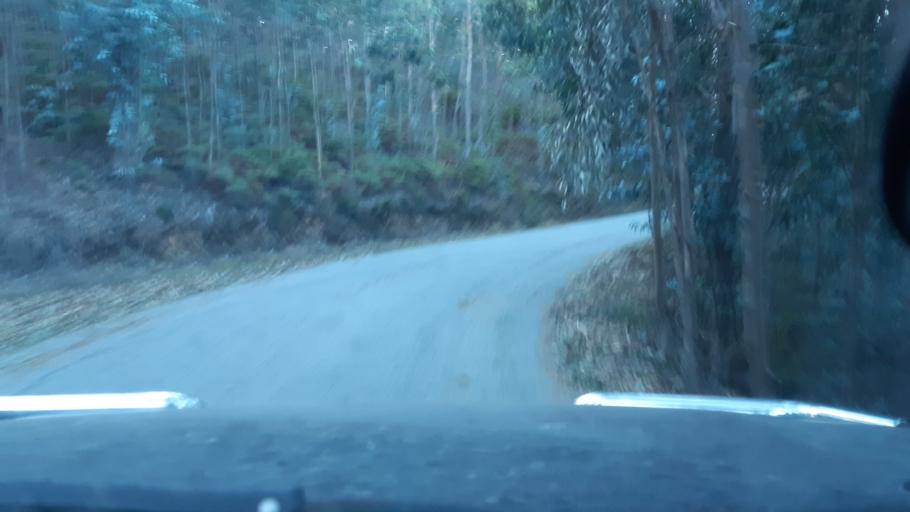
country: PT
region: Aveiro
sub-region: Agueda
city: Aguada de Cima
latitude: 40.5476
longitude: -8.2807
